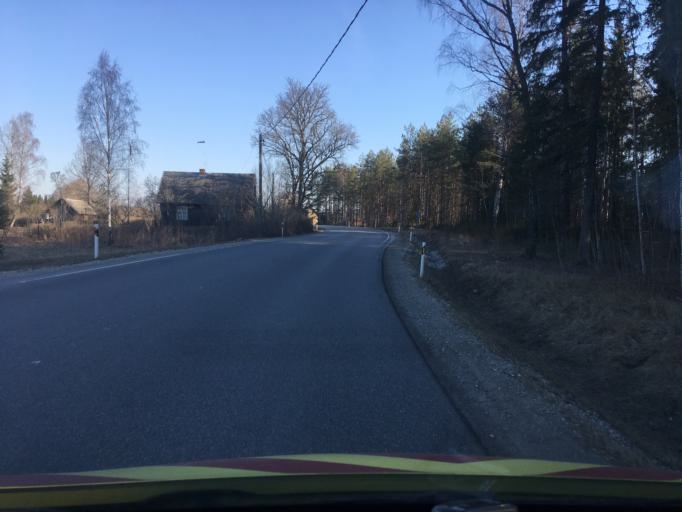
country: EE
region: Raplamaa
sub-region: Rapla vald
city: Rapla
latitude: 59.0118
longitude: 24.8373
